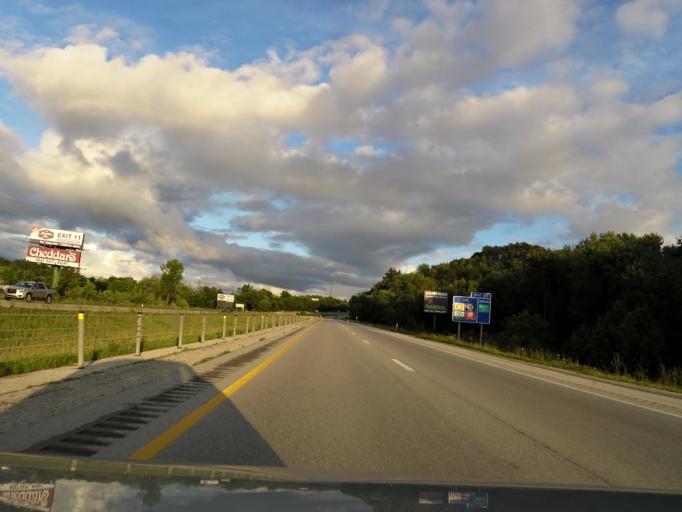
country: US
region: Kentucky
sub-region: Laurel County
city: London
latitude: 37.1647
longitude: -84.1190
